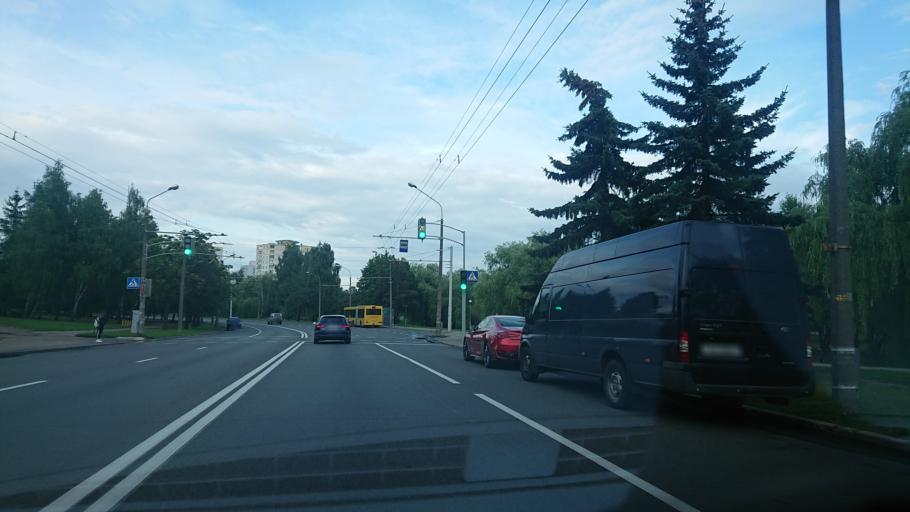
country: BY
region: Minsk
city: Borovlyany
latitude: 53.9371
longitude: 27.6410
